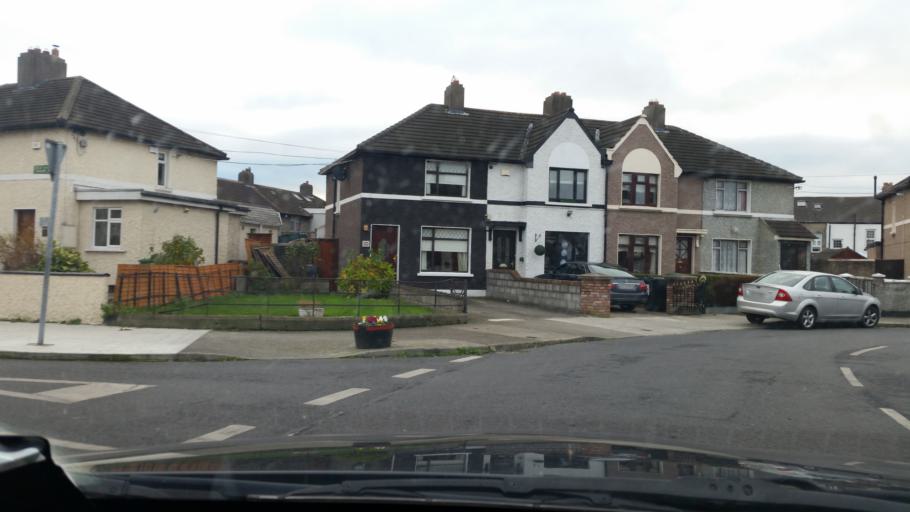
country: IE
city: Fairview
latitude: 53.3542
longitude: -6.2346
